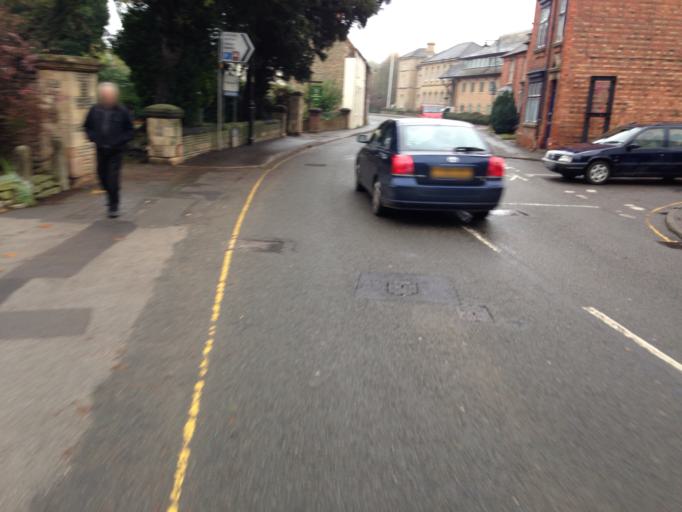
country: GB
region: England
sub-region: Lincolnshire
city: Sleaford
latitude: 52.9999
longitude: -0.4075
